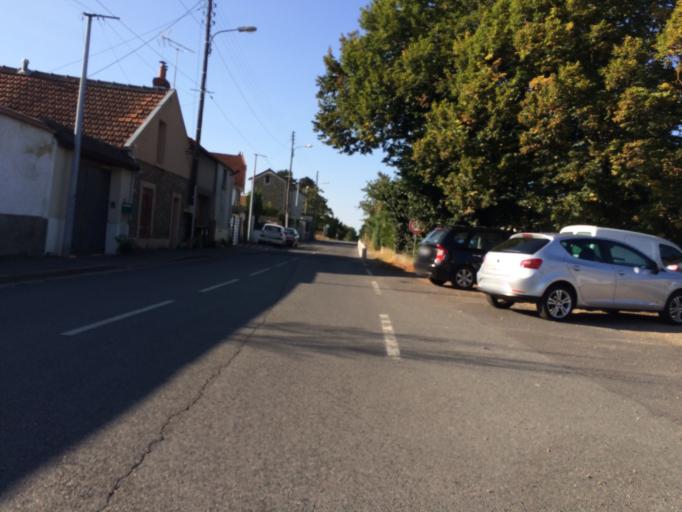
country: FR
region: Ile-de-France
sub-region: Departement de l'Essonne
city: Villiers-sur-Orge
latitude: 48.6617
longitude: 2.3080
